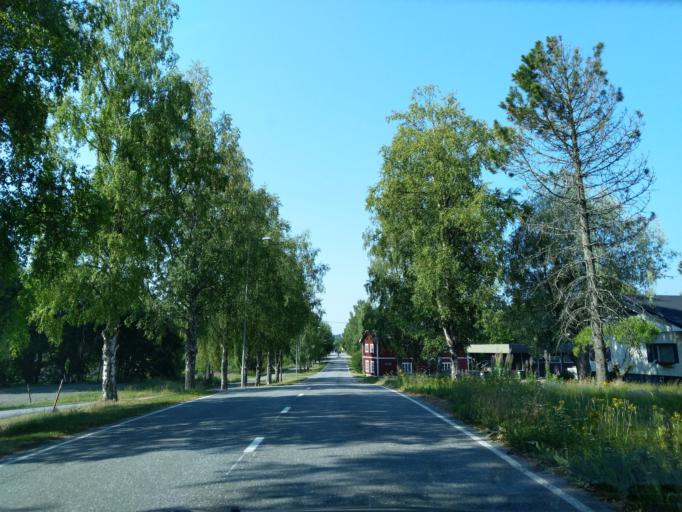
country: FI
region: Satakunta
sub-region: Pori
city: Pomarkku
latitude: 61.7006
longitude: 22.0178
